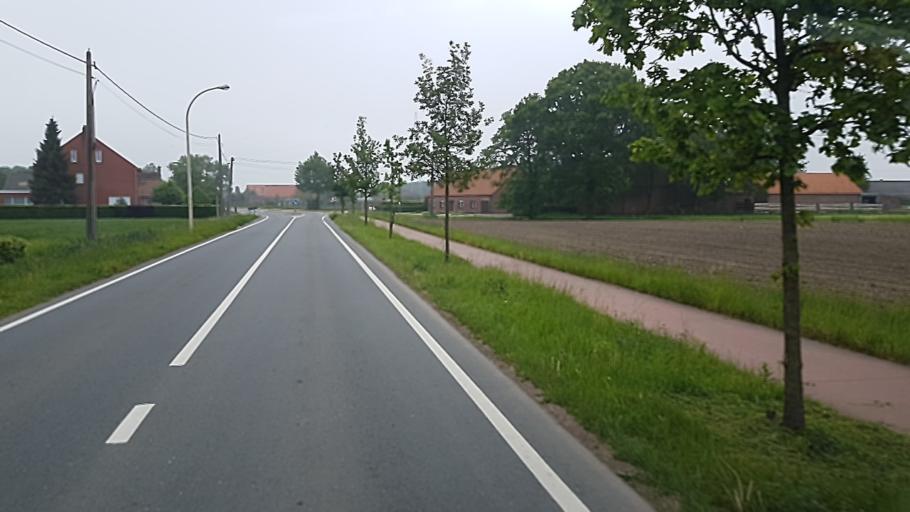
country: BE
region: Flanders
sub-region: Provincie Antwerpen
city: Brecht
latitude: 51.3239
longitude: 4.6799
